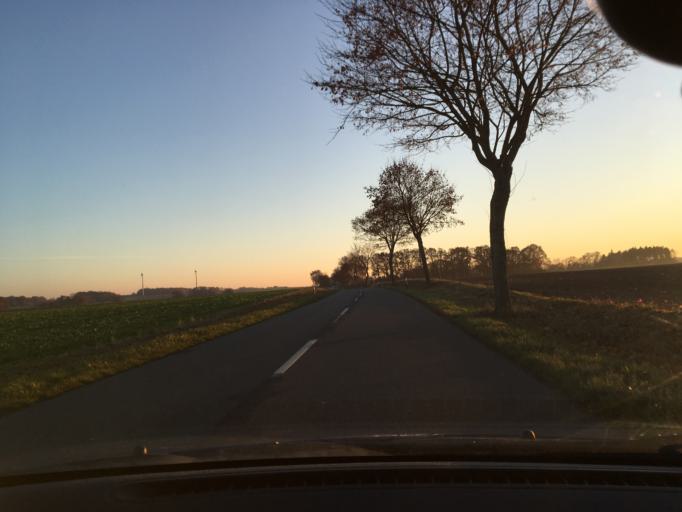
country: DE
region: Lower Saxony
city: Natendorf
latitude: 53.0692
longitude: 10.4598
